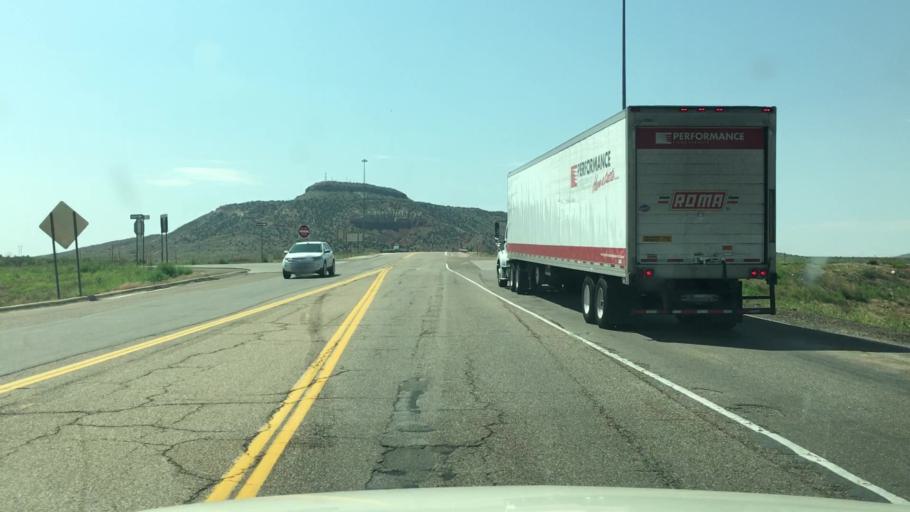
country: US
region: New Mexico
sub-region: Quay County
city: Tucumcari
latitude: 35.1582
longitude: -103.7025
